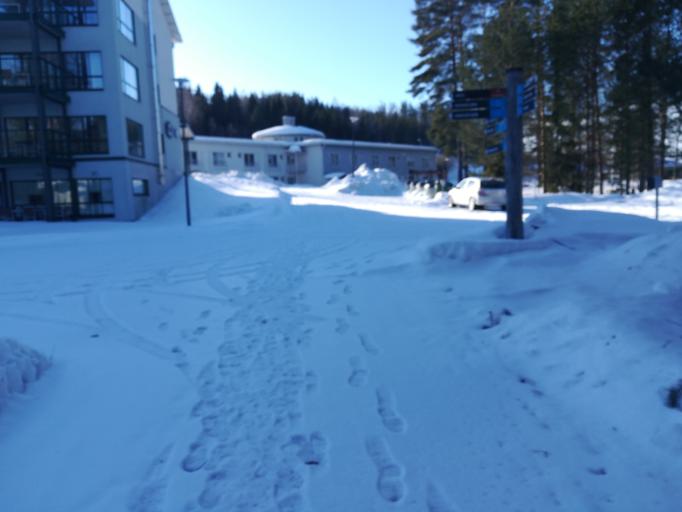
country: FI
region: Southern Savonia
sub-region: Savonlinna
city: Savonlinna
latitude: 61.8078
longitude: 29.0782
